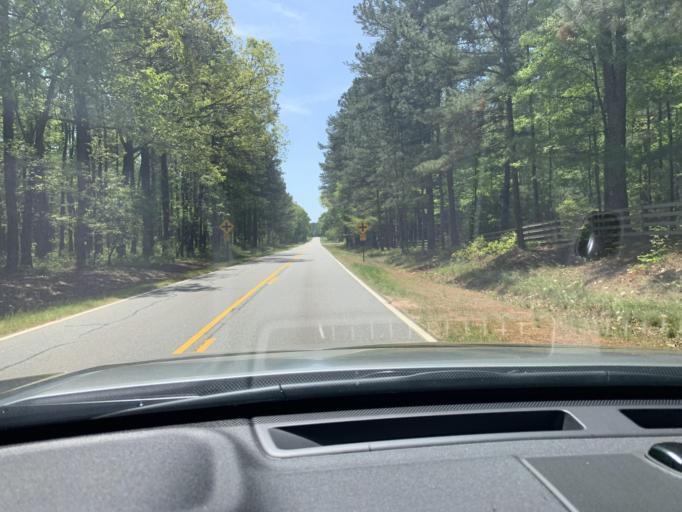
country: US
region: Georgia
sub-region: Oconee County
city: Bogart
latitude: 33.8779
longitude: -83.5552
